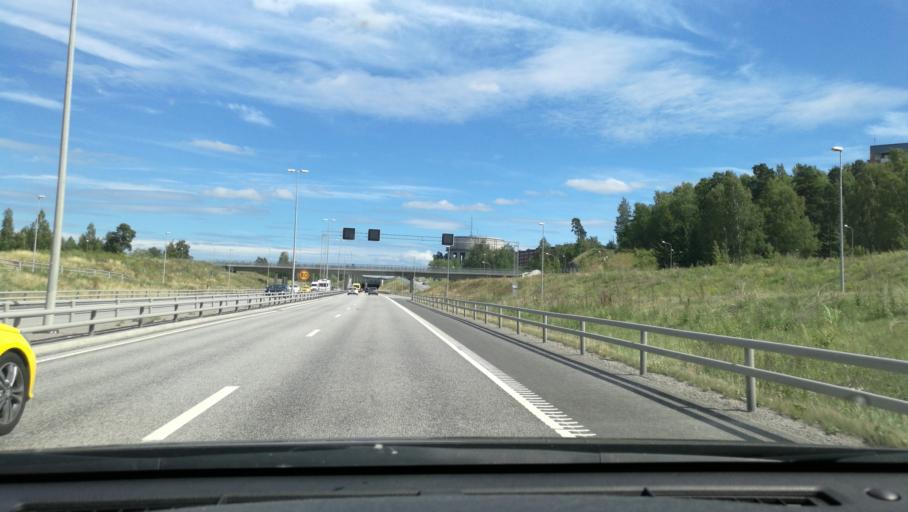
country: SE
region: Stockholm
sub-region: Jarfalla Kommun
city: Jakobsberg
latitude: 59.4000
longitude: 17.8864
